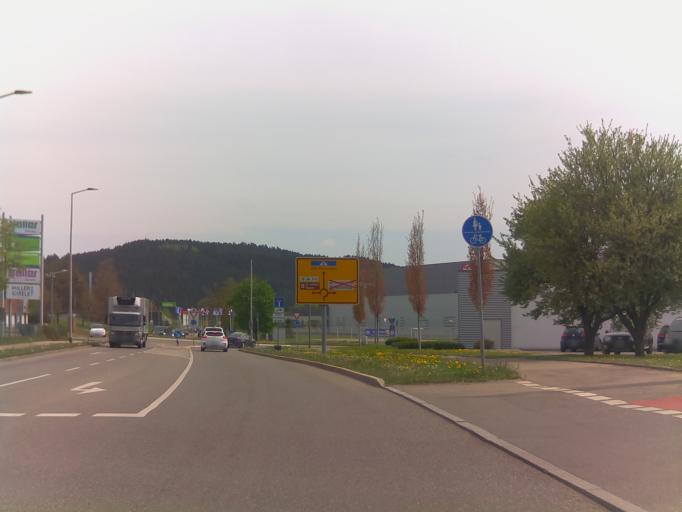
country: DE
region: Baden-Wuerttemberg
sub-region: Freiburg Region
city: Dauchingen
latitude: 48.0638
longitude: 8.5570
